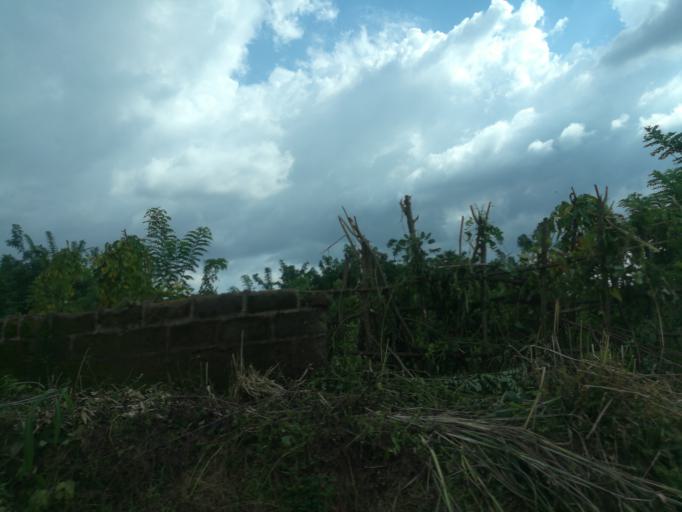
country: NG
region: Oyo
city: Ido
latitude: 7.4122
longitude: 3.8181
